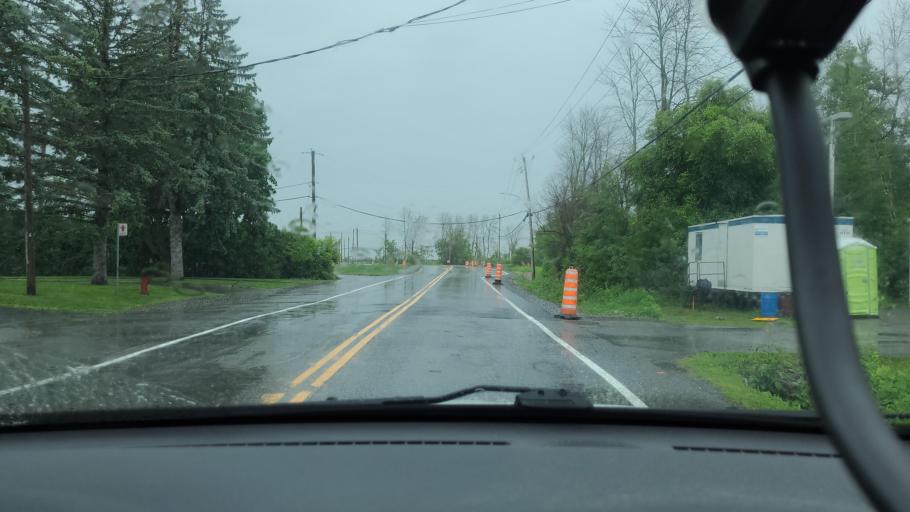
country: CA
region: Quebec
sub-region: Monteregie
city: Saint-Hyacinthe
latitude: 45.6165
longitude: -72.9848
